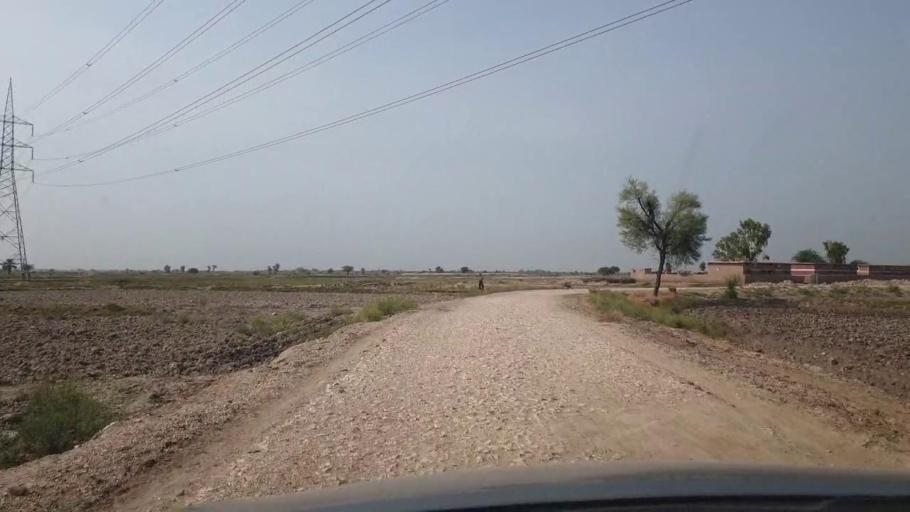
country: PK
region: Sindh
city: Lakhi
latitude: 27.8272
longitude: 68.6963
